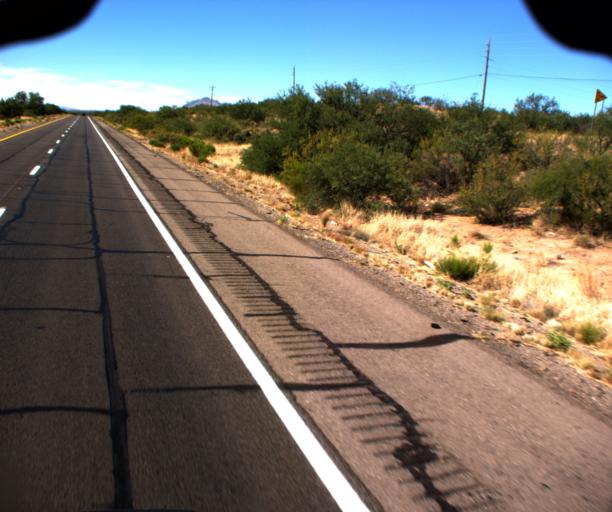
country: US
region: Arizona
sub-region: Pima County
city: Arivaca Junction
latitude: 31.6921
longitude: -111.0652
